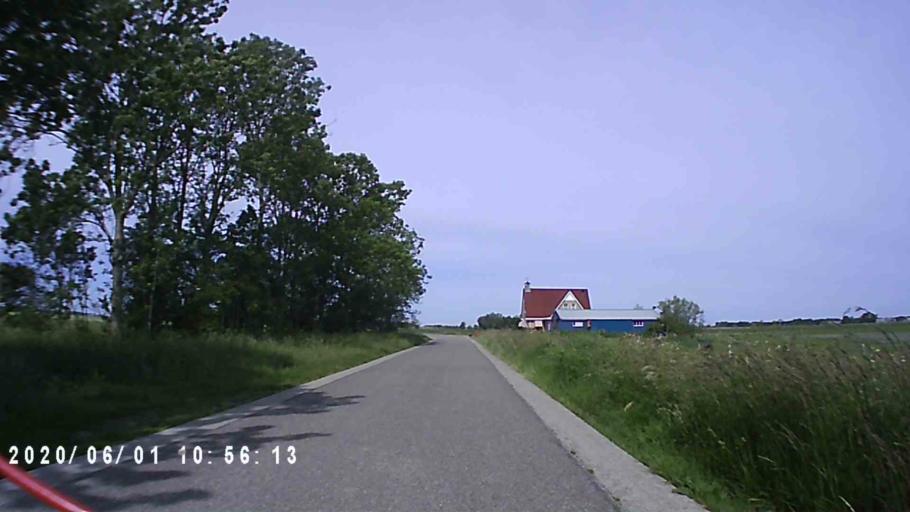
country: NL
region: Friesland
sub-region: Gemeente Franekeradeel
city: Sexbierum
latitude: 53.1987
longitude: 5.4996
